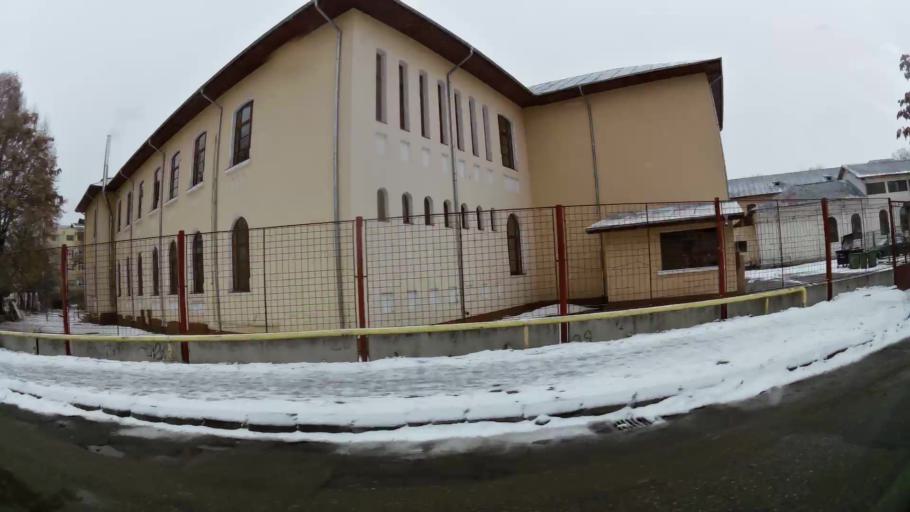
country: RO
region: Dambovita
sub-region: Municipiul Targoviste
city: Targoviste
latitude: 44.9297
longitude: 25.4516
